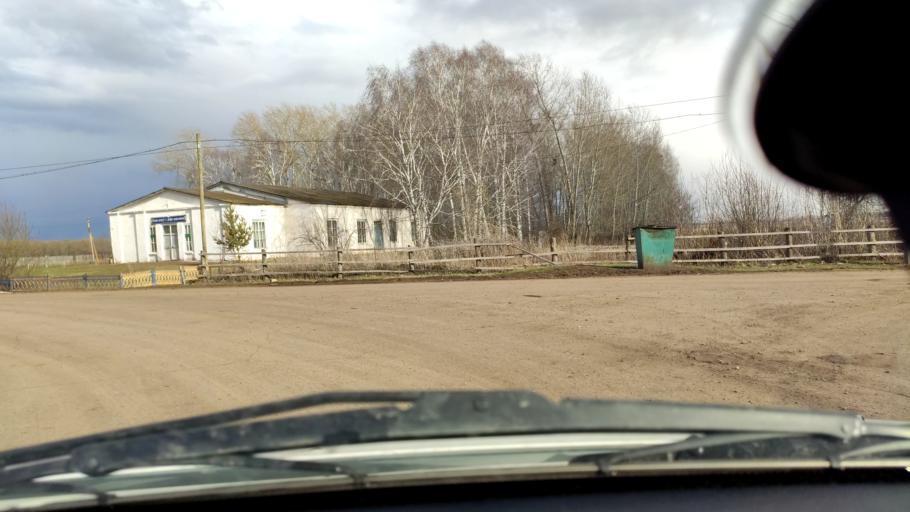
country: RU
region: Bashkortostan
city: Buzdyak
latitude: 54.7647
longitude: 54.6175
